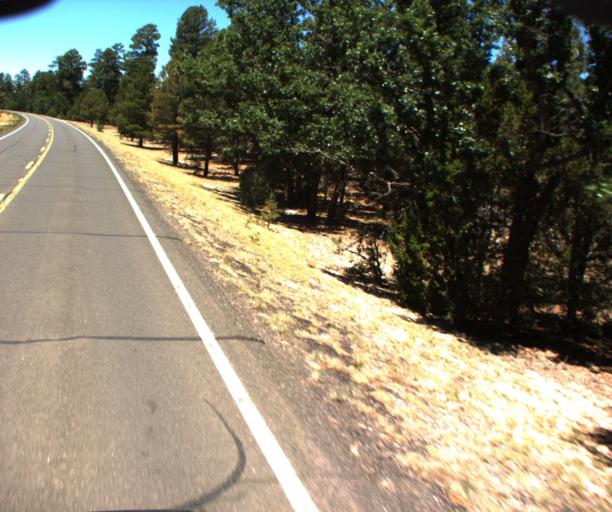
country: US
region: Arizona
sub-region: Gila County
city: Star Valley
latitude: 34.6270
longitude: -111.1386
